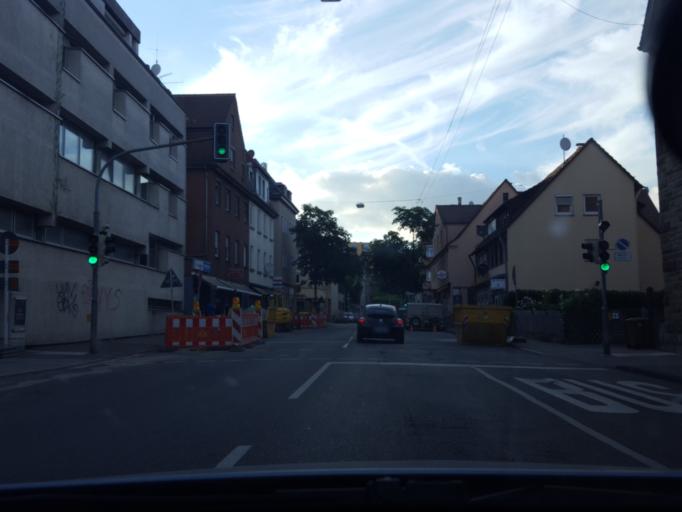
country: DE
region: Baden-Wuerttemberg
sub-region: Regierungsbezirk Stuttgart
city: Stuttgart-Ost
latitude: 48.8075
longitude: 9.2109
